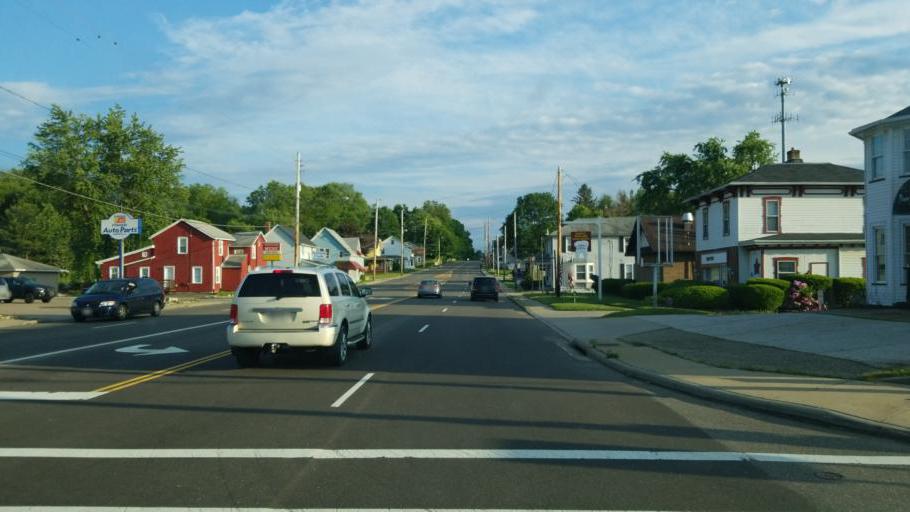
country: US
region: Ohio
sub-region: Stark County
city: Uniontown
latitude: 40.9760
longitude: -81.4071
